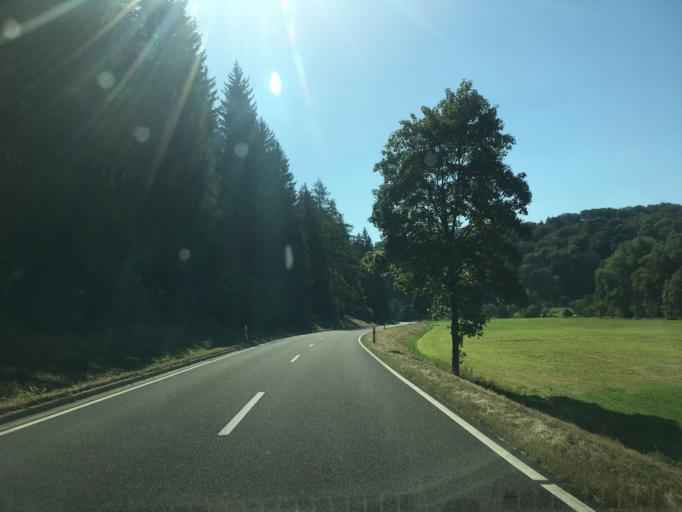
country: DE
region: Baden-Wuerttemberg
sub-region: Tuebingen Region
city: Munsingen
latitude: 48.3507
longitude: 9.4853
